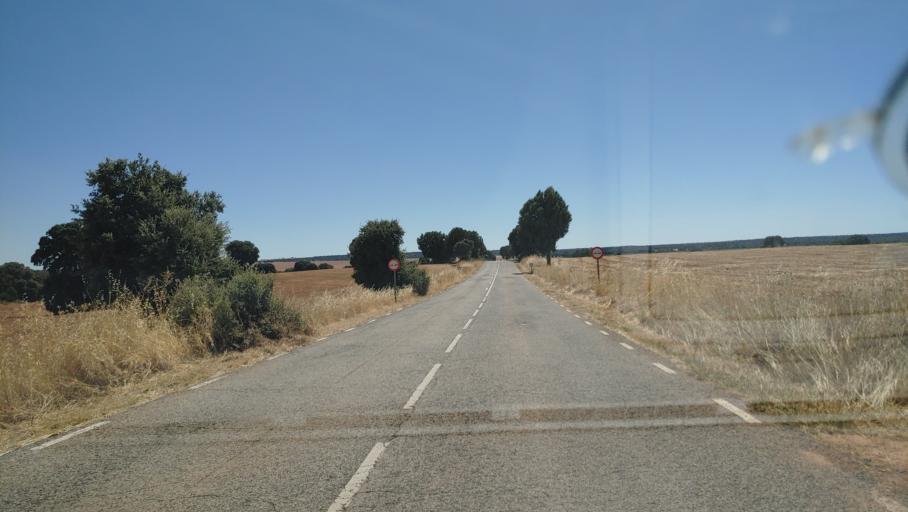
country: ES
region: Castille-La Mancha
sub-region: Provincia de Albacete
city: Ossa de Montiel
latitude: 38.9089
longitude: -2.7600
